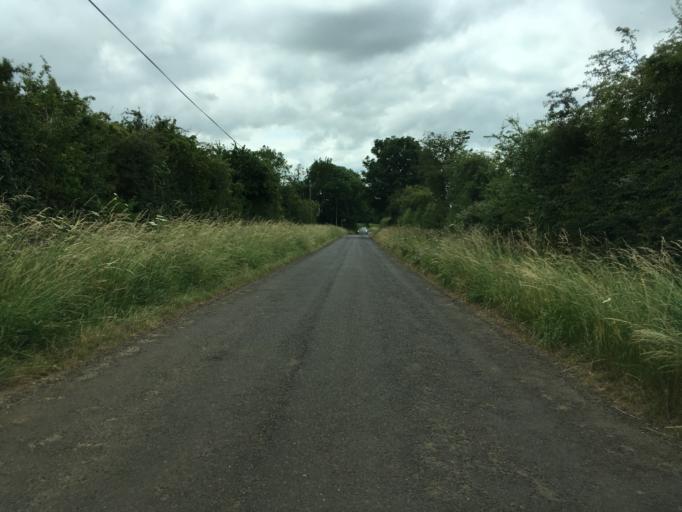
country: GB
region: England
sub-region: Oxfordshire
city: Hook Norton
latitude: 51.9399
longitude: -1.4491
